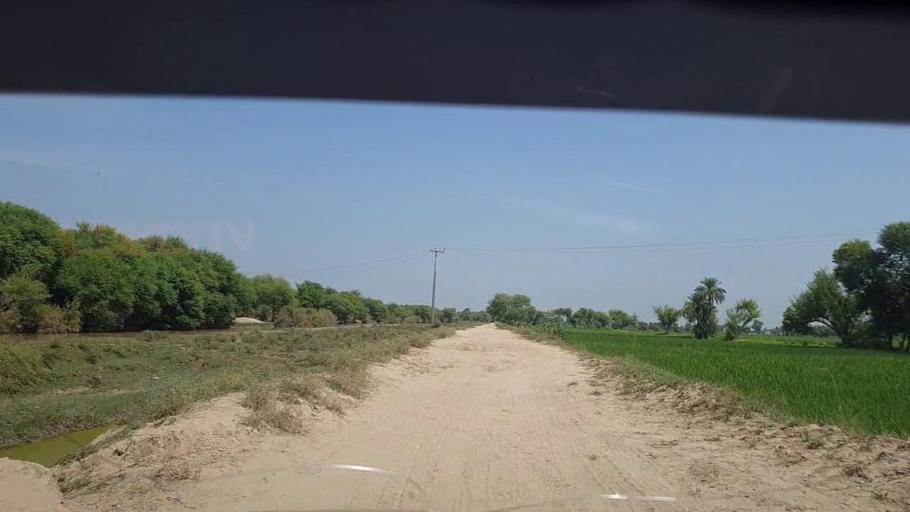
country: PK
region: Sindh
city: Tangwani
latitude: 28.2317
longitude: 68.9406
